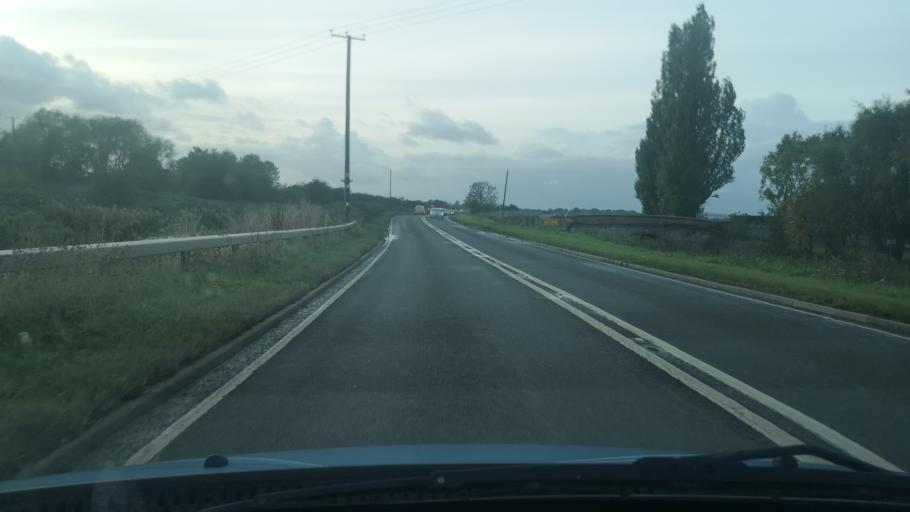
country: GB
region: England
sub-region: North Lincolnshire
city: Belton
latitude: 53.5798
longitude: -0.7812
